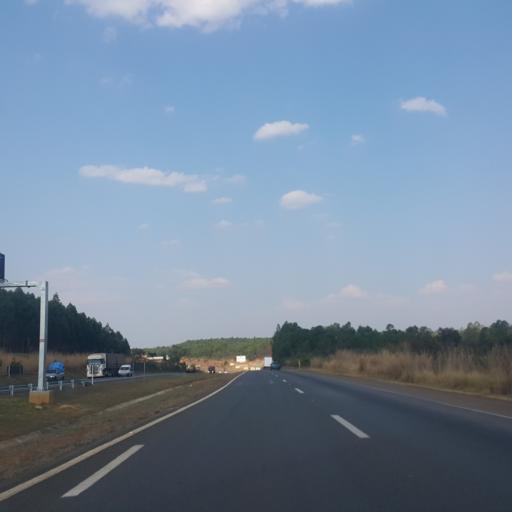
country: BR
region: Goias
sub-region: Abadiania
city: Abadiania
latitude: -16.1893
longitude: -48.6822
